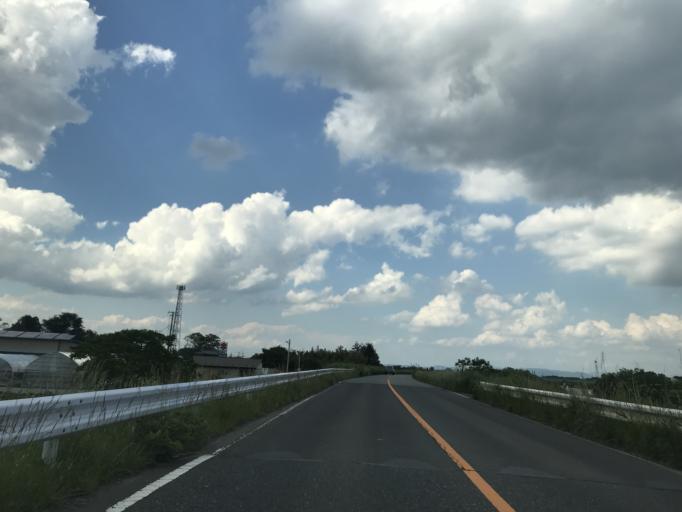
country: JP
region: Miyagi
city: Wakuya
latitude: 38.6380
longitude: 141.2049
